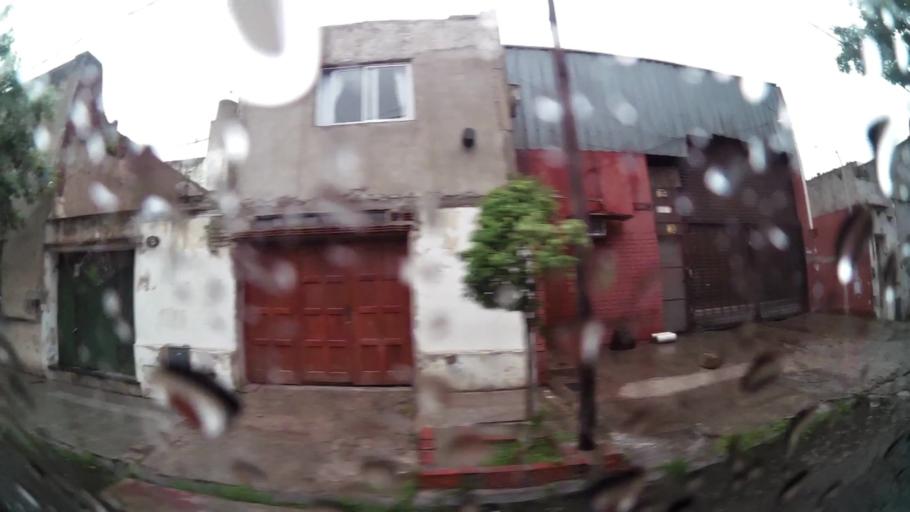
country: AR
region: Buenos Aires
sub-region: Partido de Avellaneda
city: Avellaneda
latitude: -34.6464
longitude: -58.3670
